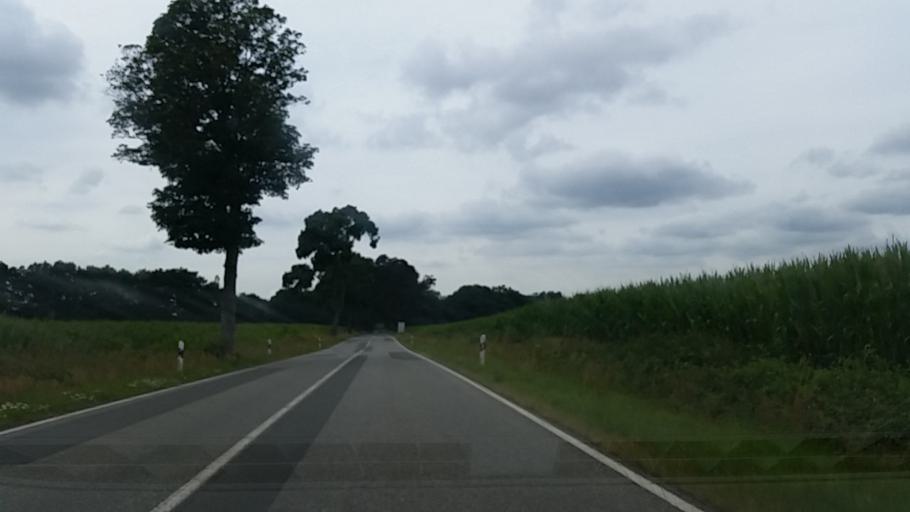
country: DE
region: Mecklenburg-Vorpommern
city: Lubtheen
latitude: 53.3961
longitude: 10.9896
